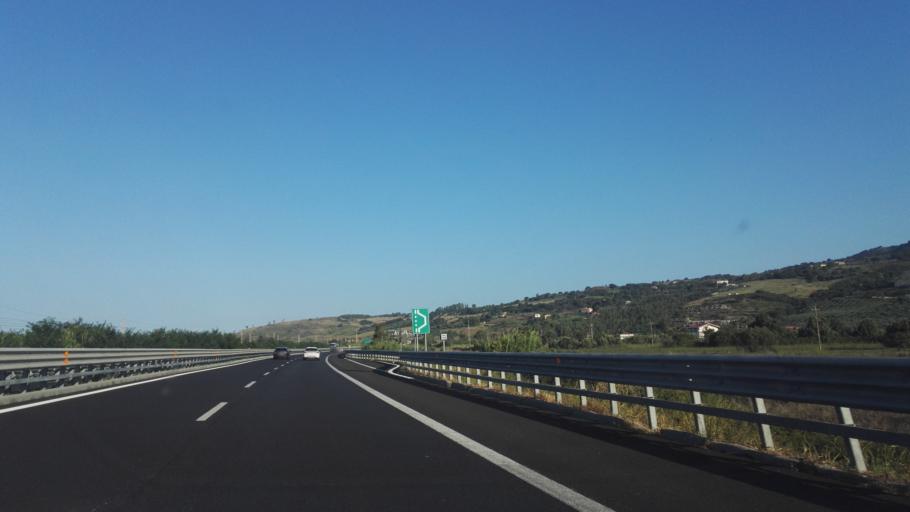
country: IT
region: Calabria
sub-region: Provincia di Catanzaro
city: Gizzeria
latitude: 38.9430
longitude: 16.1937
